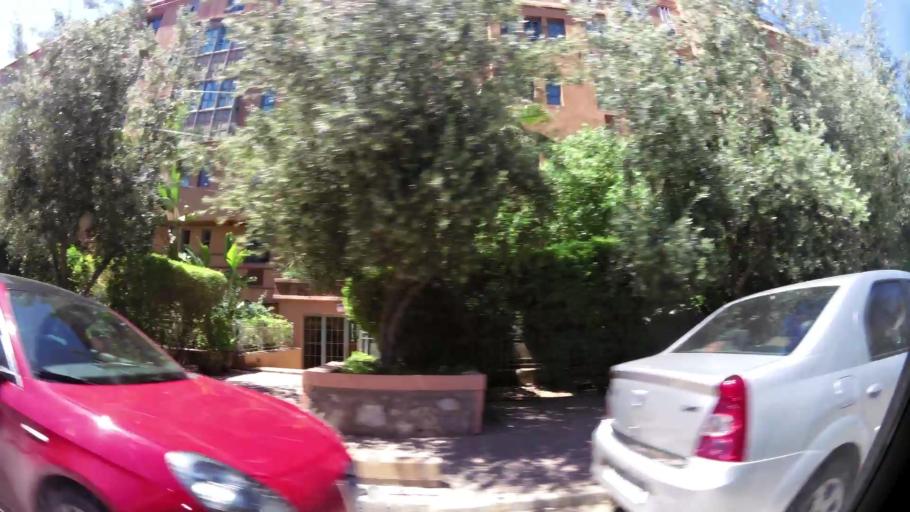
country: MA
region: Marrakech-Tensift-Al Haouz
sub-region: Marrakech
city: Marrakesh
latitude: 31.6234
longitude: -8.0015
